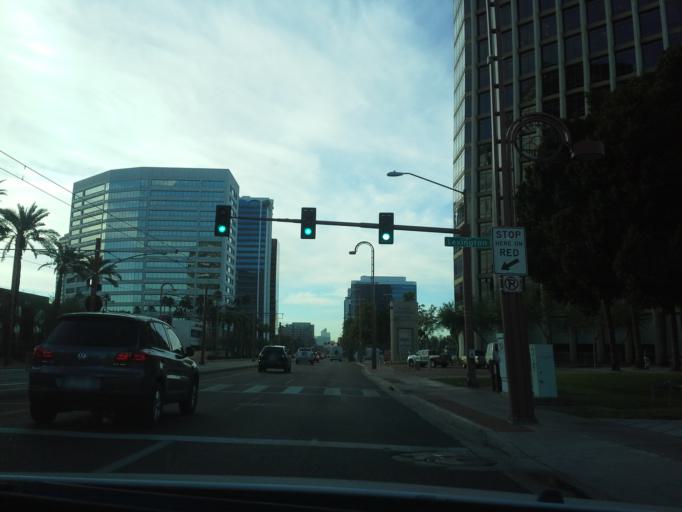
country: US
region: Arizona
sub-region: Maricopa County
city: Phoenix
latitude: 33.4866
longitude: -112.0740
